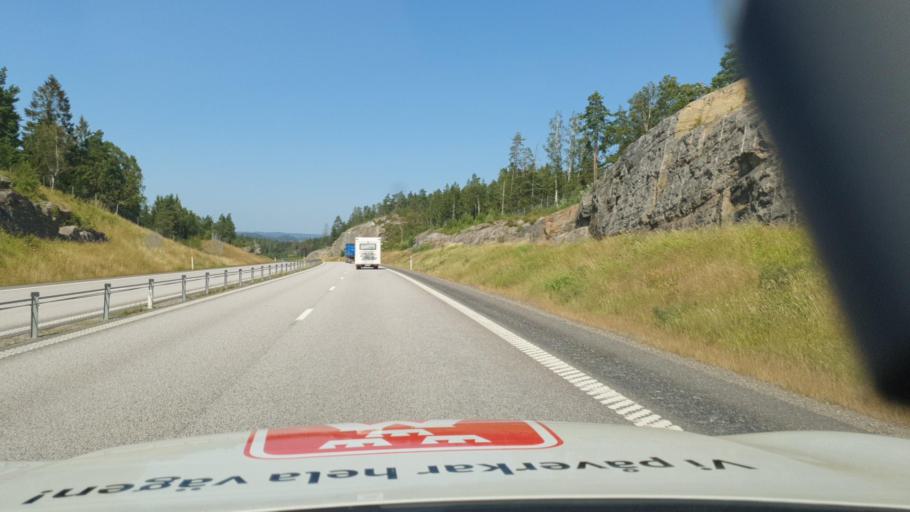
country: SE
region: Vaestra Goetaland
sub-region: Lilla Edets Kommun
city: Lodose
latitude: 58.0571
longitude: 12.1679
